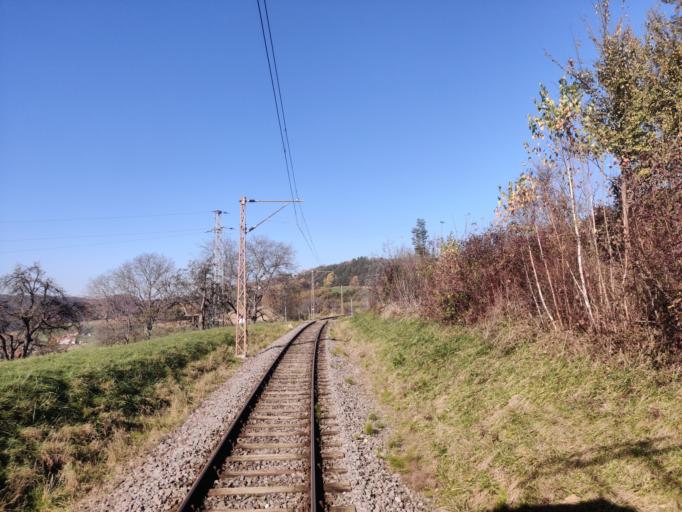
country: AT
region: Styria
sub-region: Politischer Bezirk Suedoststeiermark
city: Trautmannsdorf in Oststeiermark
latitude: 46.8813
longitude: 15.8834
